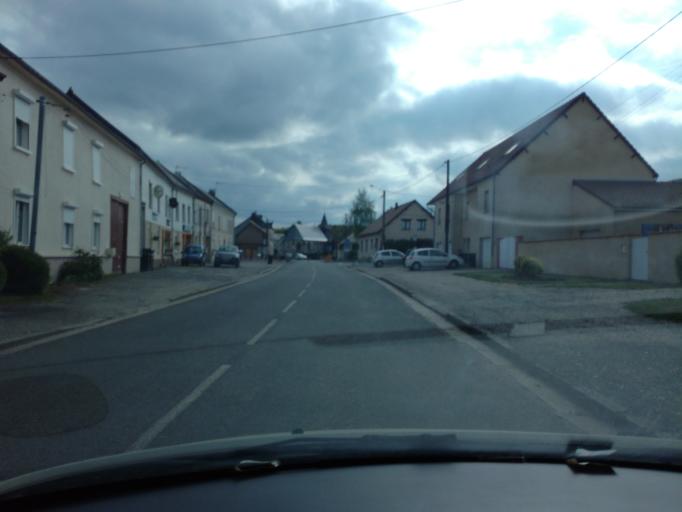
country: FR
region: Picardie
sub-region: Departement de la Somme
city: Poix-de-Picardie
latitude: 49.7915
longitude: 1.9924
